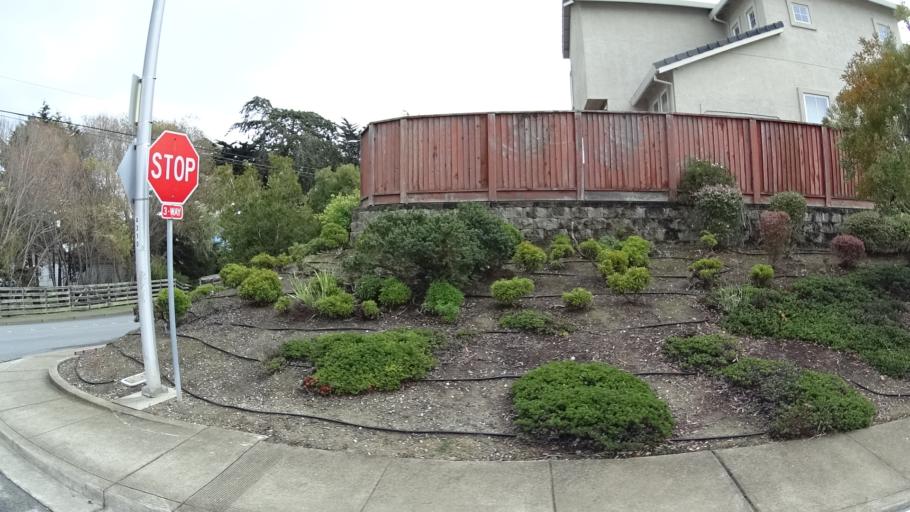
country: US
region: California
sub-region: San Mateo County
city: San Bruno
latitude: 37.6431
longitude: -122.4344
